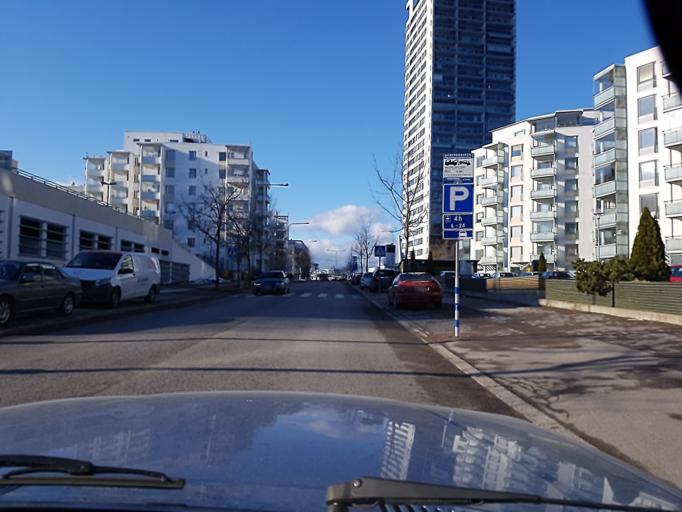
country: FI
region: Uusimaa
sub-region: Helsinki
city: Vantaa
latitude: 60.2046
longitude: 25.1459
